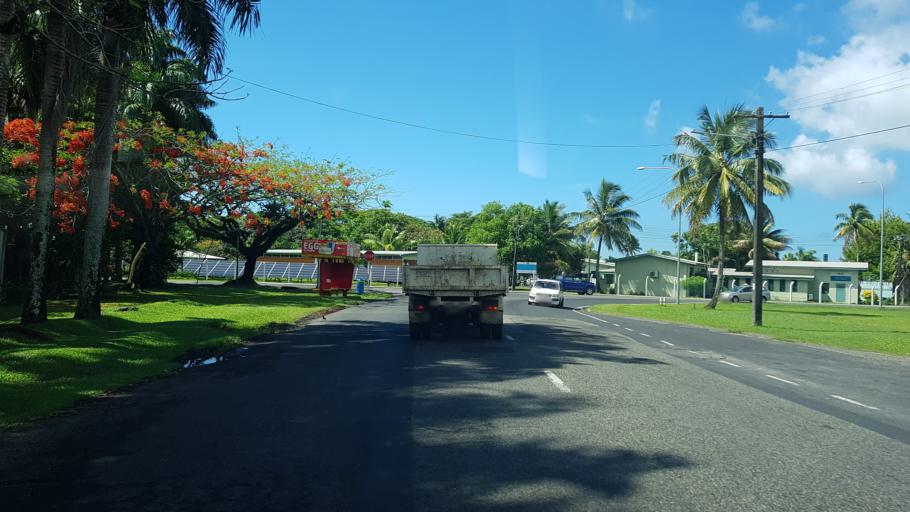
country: FJ
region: Central
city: Suva
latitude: -18.1483
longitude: 178.4528
